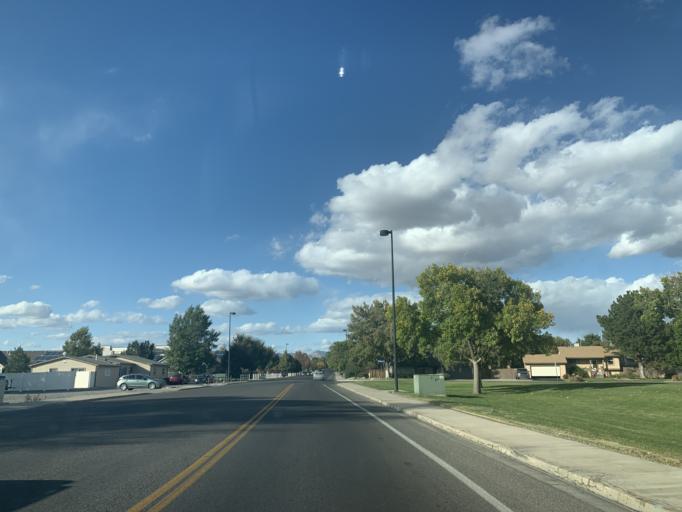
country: US
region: Colorado
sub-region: Mesa County
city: Grand Junction
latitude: 39.0924
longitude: -108.5430
